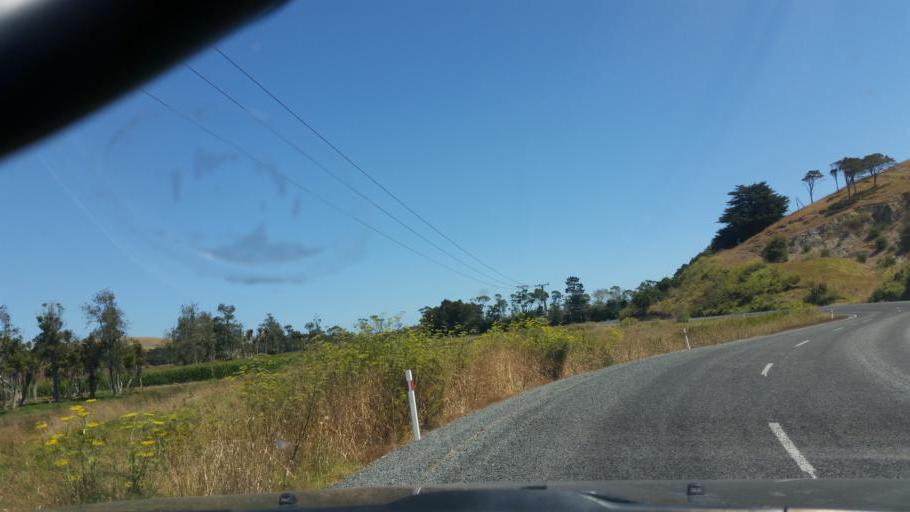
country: NZ
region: Northland
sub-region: Kaipara District
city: Dargaville
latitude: -36.0062
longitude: 173.9616
